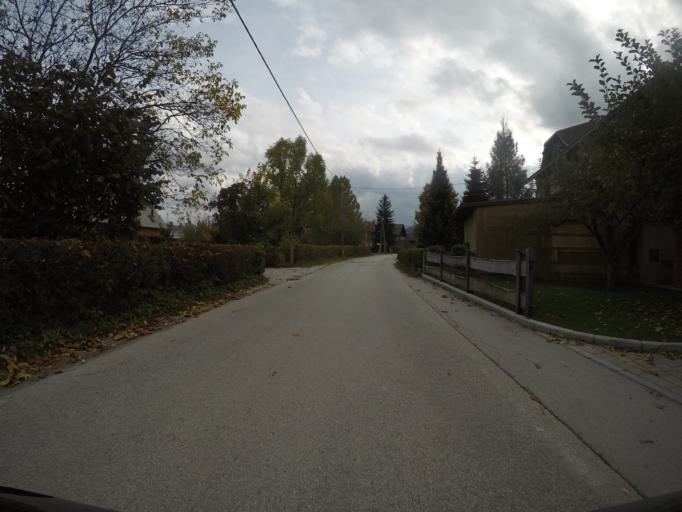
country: SI
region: Bled
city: Bled
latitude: 46.3759
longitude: 14.1043
